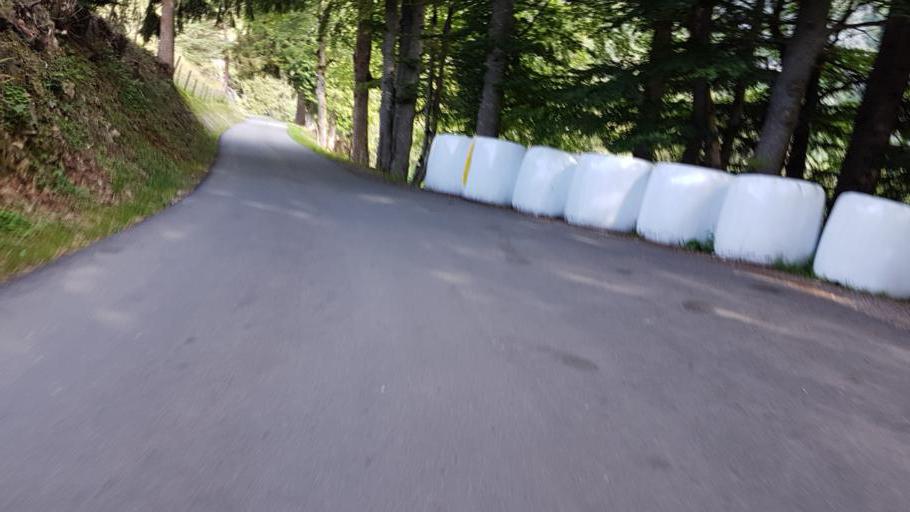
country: CH
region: Bern
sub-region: Obersimmental-Saanen District
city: Boltigen
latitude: 46.6651
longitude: 7.4618
